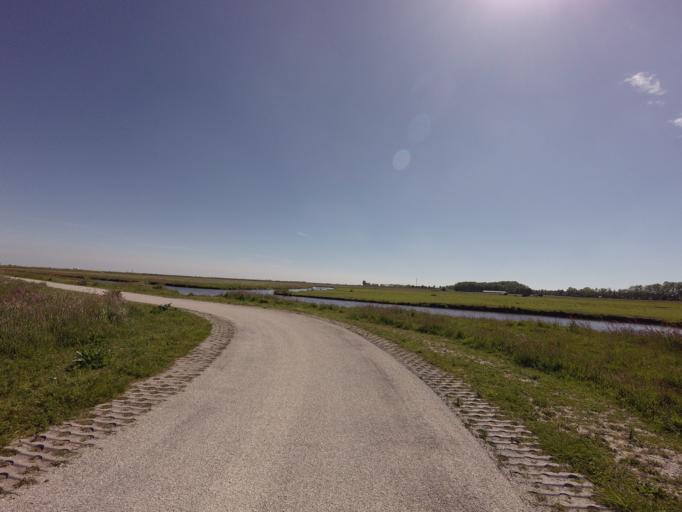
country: NL
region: North Holland
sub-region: Gemeente Uitgeest
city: Uitgeest
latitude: 52.5603
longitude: 4.7395
